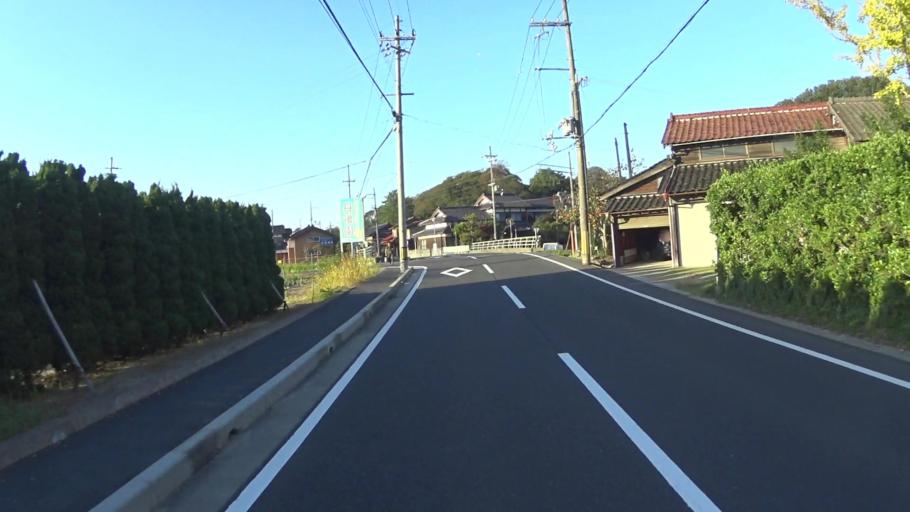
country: JP
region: Hyogo
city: Toyooka
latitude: 35.6529
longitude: 134.9698
